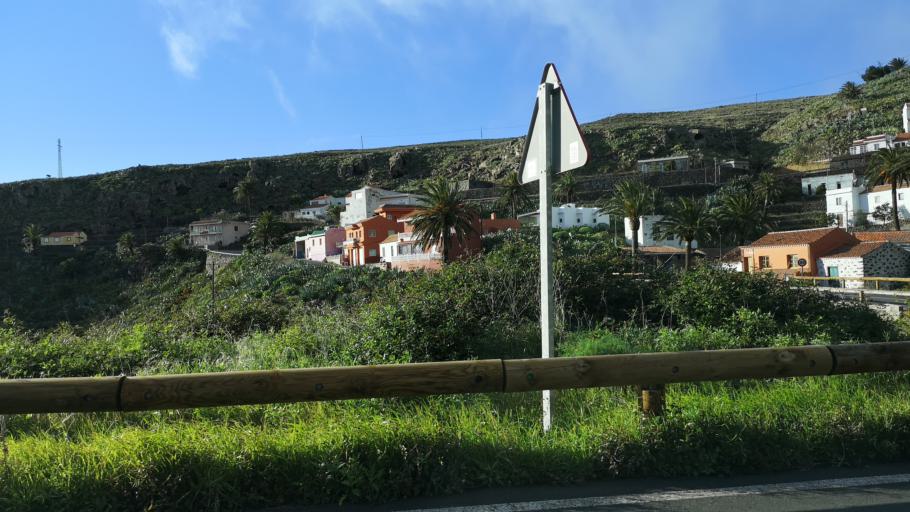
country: ES
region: Canary Islands
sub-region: Provincia de Santa Cruz de Tenerife
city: Vallehermosa
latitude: 28.1322
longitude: -17.3202
